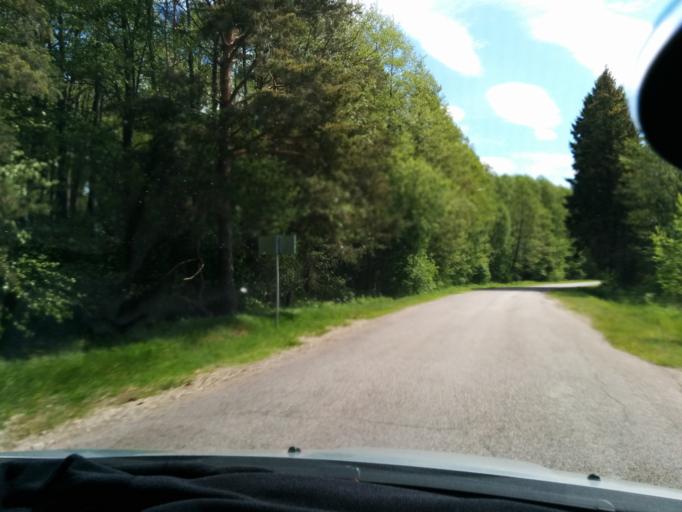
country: EE
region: Harju
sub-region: Loksa linn
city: Loksa
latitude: 59.5806
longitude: 25.9162
